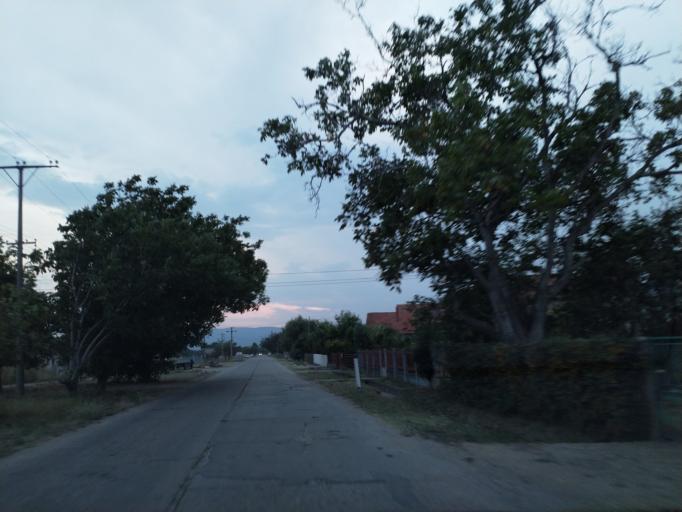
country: RS
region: Central Serbia
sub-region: Pomoravski Okrug
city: Paracin
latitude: 43.8662
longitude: 21.4452
